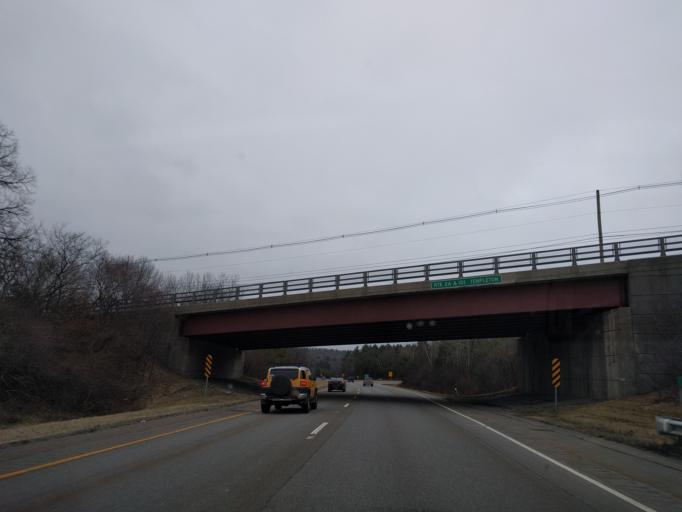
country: US
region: Massachusetts
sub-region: Worcester County
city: Templeton
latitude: 42.5583
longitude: -72.0483
